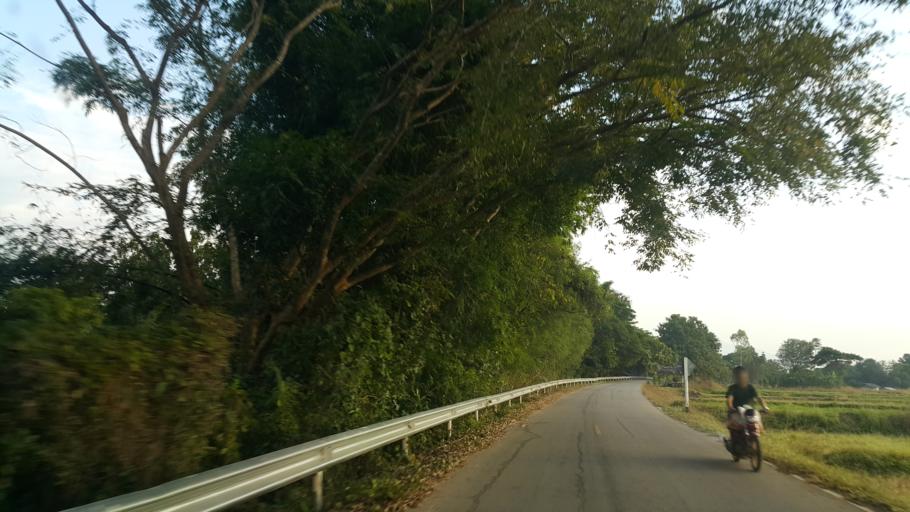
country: TH
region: Lampang
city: Sop Prap
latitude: 17.9145
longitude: 99.3302
